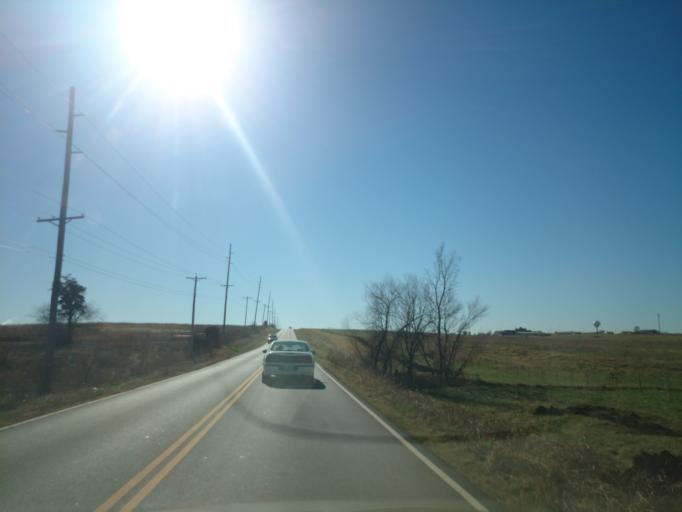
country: US
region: Oklahoma
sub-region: Payne County
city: Stillwater
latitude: 36.1408
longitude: -97.0874
